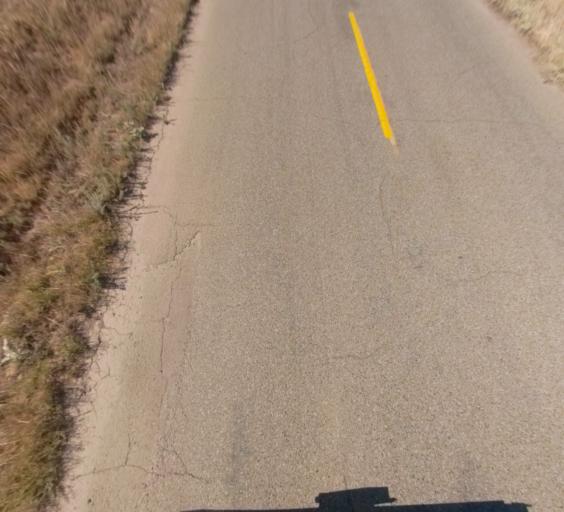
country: US
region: California
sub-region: Madera County
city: Bonadelle Ranchos-Madera Ranchos
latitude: 36.8934
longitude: -119.8109
